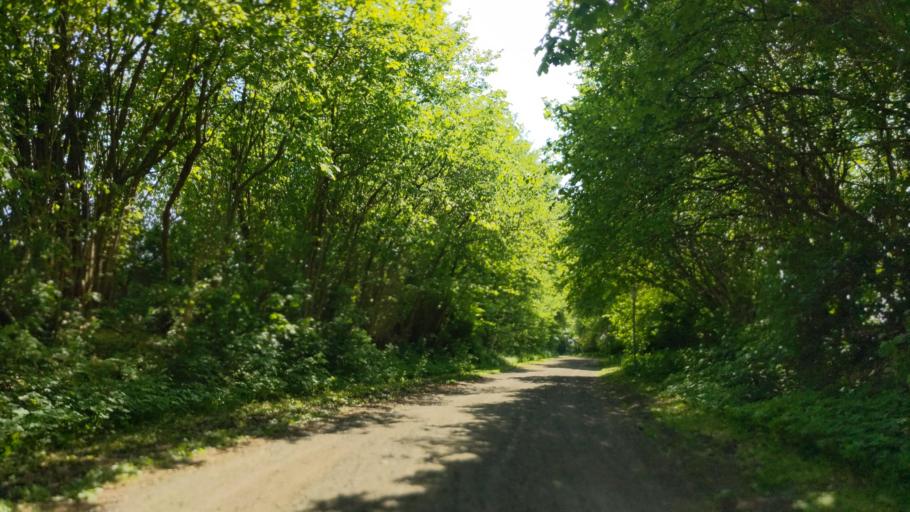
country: DE
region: Mecklenburg-Vorpommern
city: Selmsdorf
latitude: 53.8761
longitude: 10.8621
